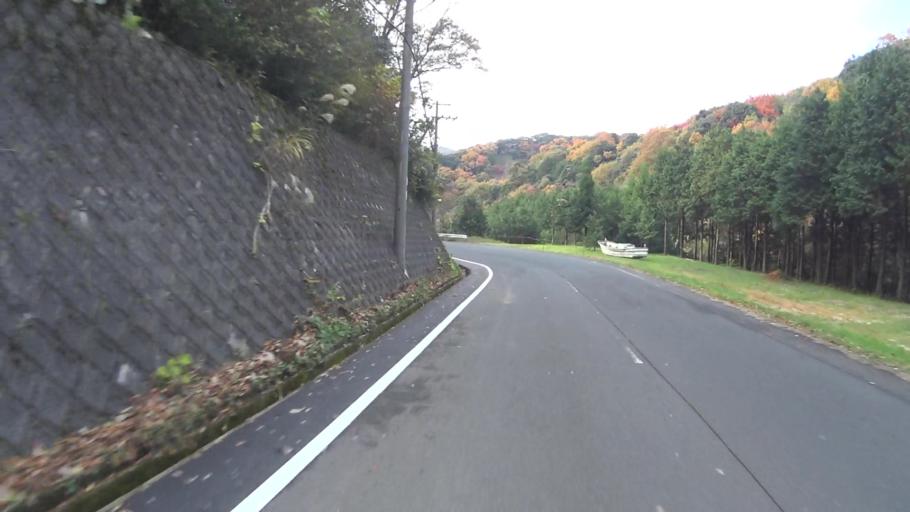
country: JP
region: Kyoto
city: Maizuru
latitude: 35.5628
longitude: 135.4347
